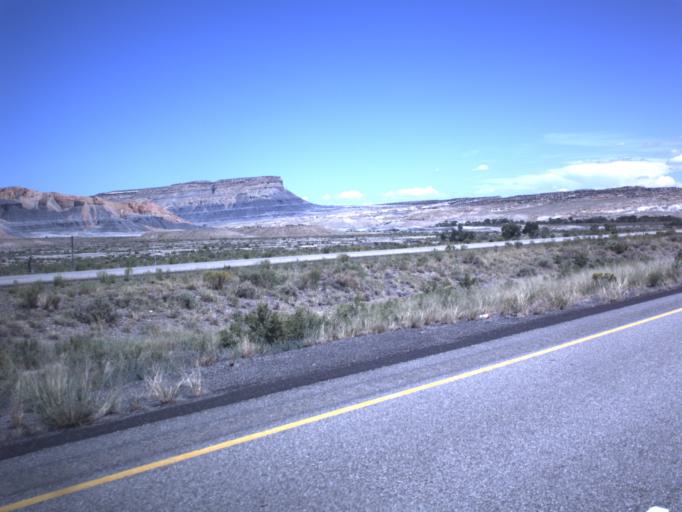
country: US
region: Utah
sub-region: Emery County
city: Ferron
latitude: 38.8102
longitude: -111.2195
